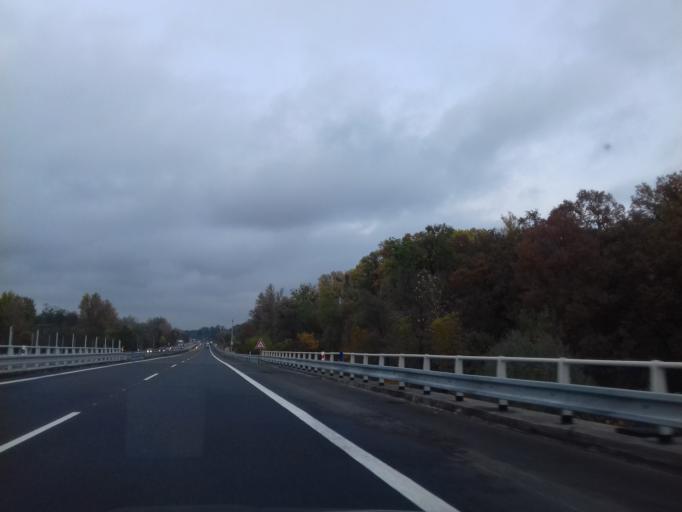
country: CZ
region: South Moravian
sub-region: Okres Breclav
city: Lanzhot
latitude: 48.6915
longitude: 16.9875
